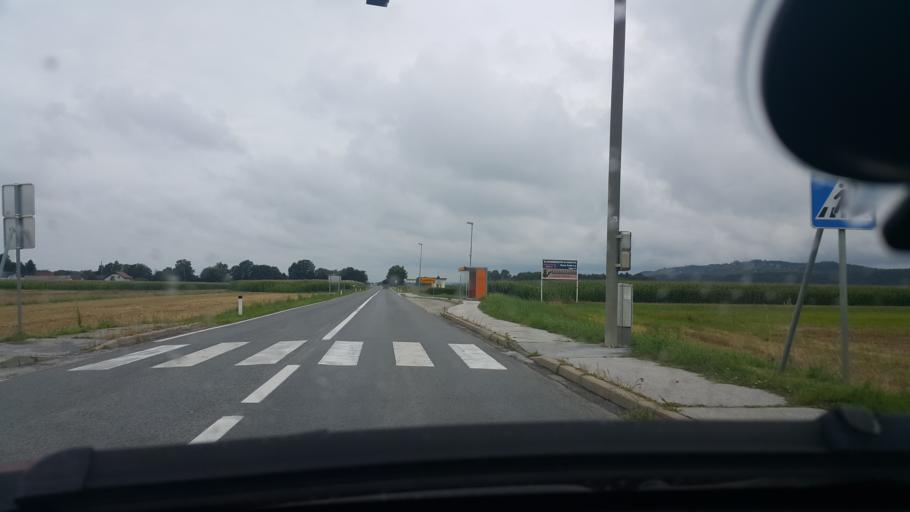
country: SI
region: Zavrc
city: Zavrc
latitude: 46.4140
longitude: 16.0639
